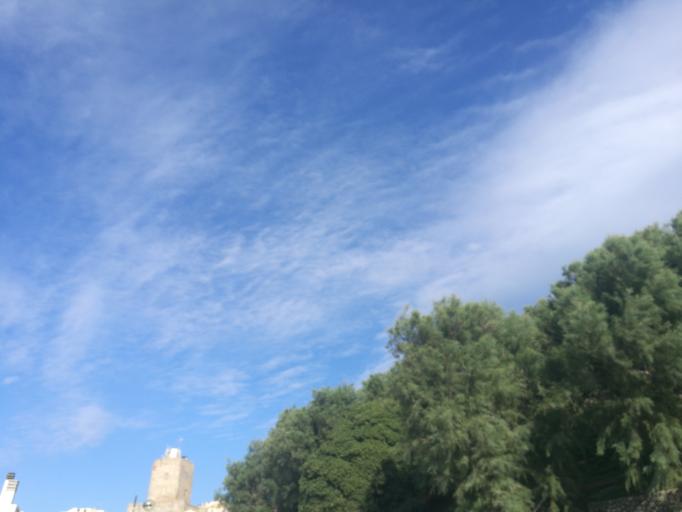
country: IT
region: Molise
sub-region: Provincia di Campobasso
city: Termoli
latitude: 42.0040
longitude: 14.9937
